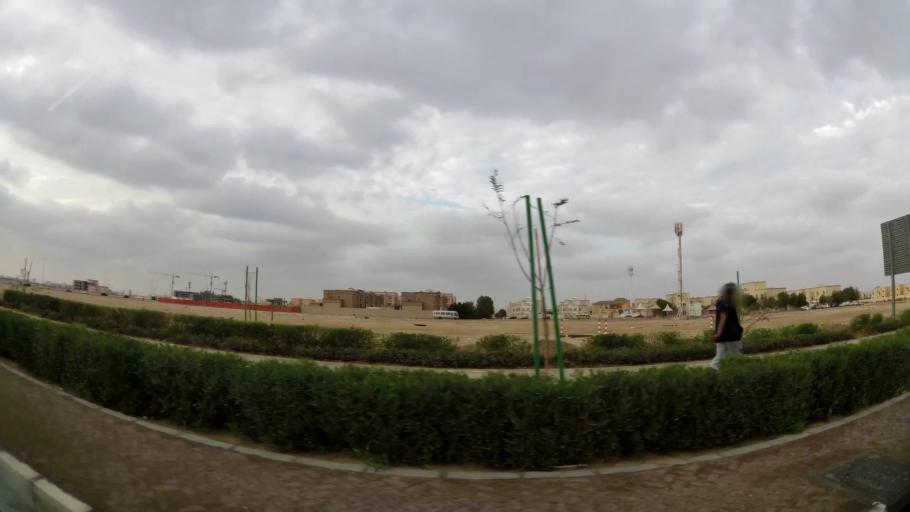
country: AE
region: Abu Dhabi
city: Abu Dhabi
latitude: 24.3475
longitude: 54.5444
